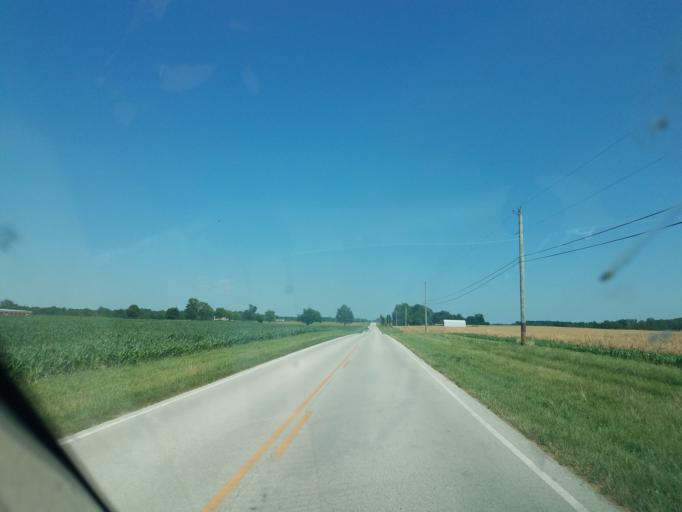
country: US
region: Ohio
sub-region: Wyandot County
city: Upper Sandusky
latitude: 40.8259
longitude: -83.2191
